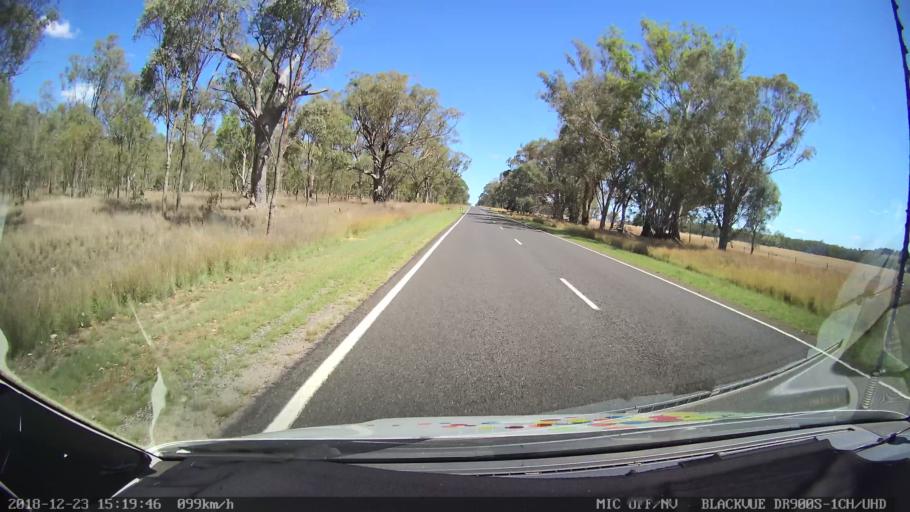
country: AU
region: New South Wales
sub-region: Tamworth Municipality
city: Manilla
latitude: -30.8334
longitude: 150.7850
